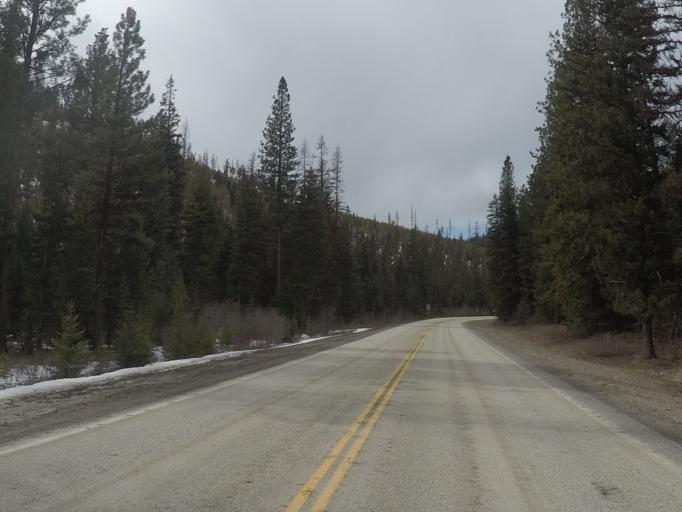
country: US
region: Montana
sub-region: Missoula County
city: Frenchtown
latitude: 46.7659
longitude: -114.4743
